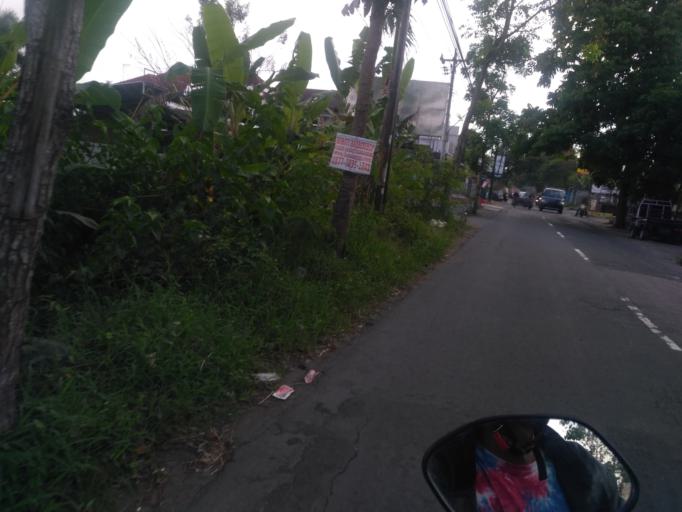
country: ID
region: Daerah Istimewa Yogyakarta
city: Yogyakarta
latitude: -7.7662
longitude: 110.3442
